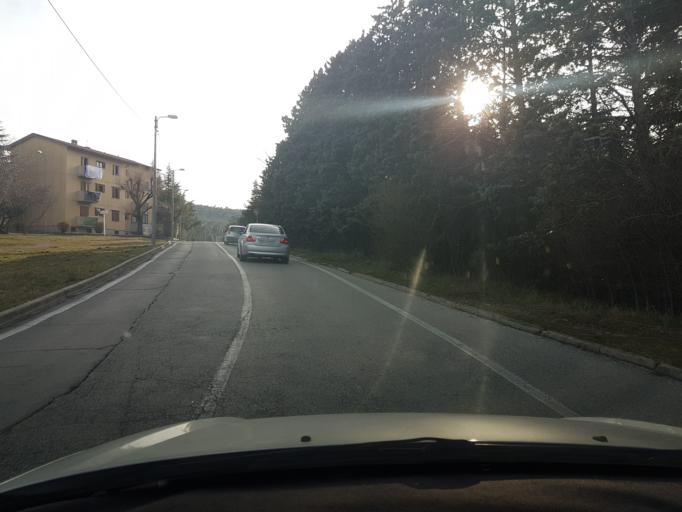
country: IT
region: Friuli Venezia Giulia
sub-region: Provincia di Trieste
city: Villa Opicina
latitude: 45.6914
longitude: 13.7751
